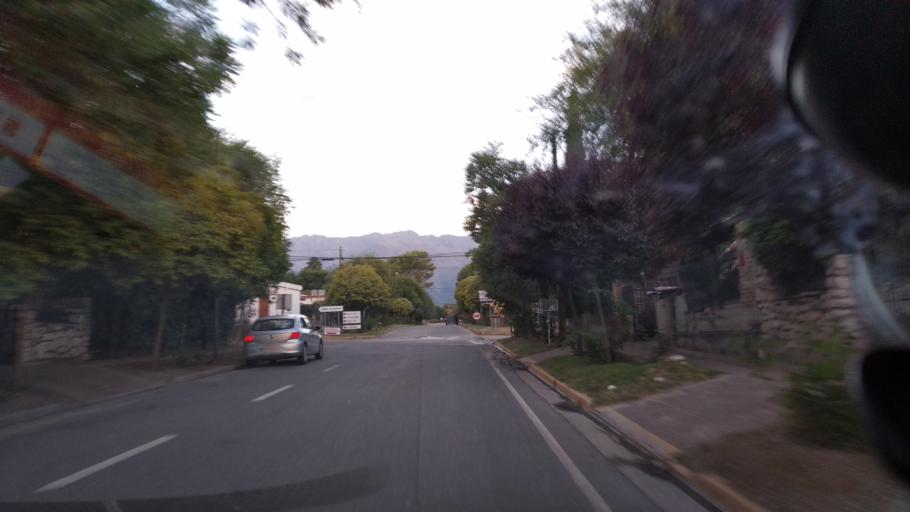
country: AR
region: Cordoba
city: Villa Las Rosas
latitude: -31.9521
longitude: -65.0539
